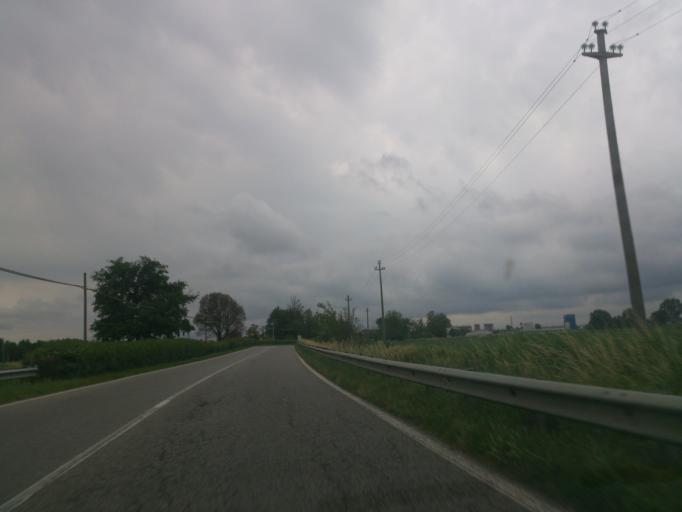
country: IT
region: Lombardy
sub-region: Citta metropolitana di Milano
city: Triginto
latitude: 45.4097
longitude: 9.3164
